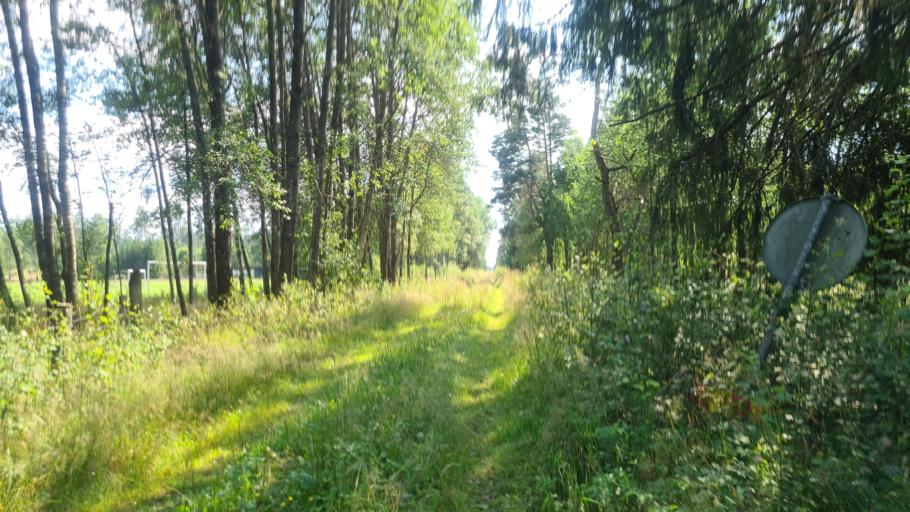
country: SE
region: Kronoberg
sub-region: Ljungby Kommun
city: Ljungby
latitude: 56.7637
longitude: 13.8923
